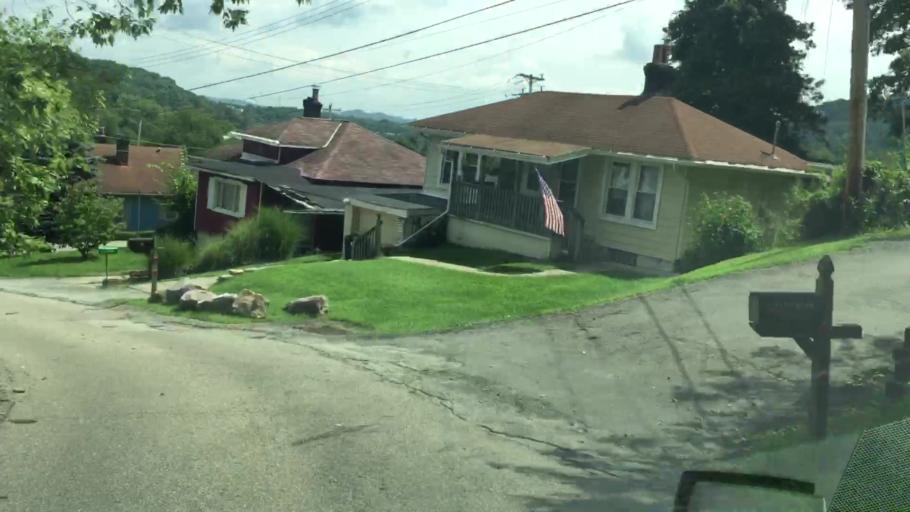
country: US
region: Pennsylvania
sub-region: Allegheny County
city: Russellton
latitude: 40.5695
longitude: -79.8643
